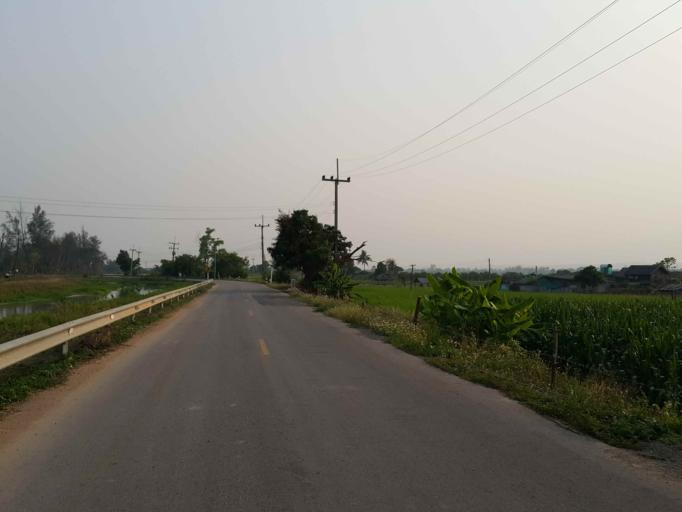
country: TH
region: Chiang Mai
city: Mae Taeng
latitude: 19.0174
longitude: 98.9856
